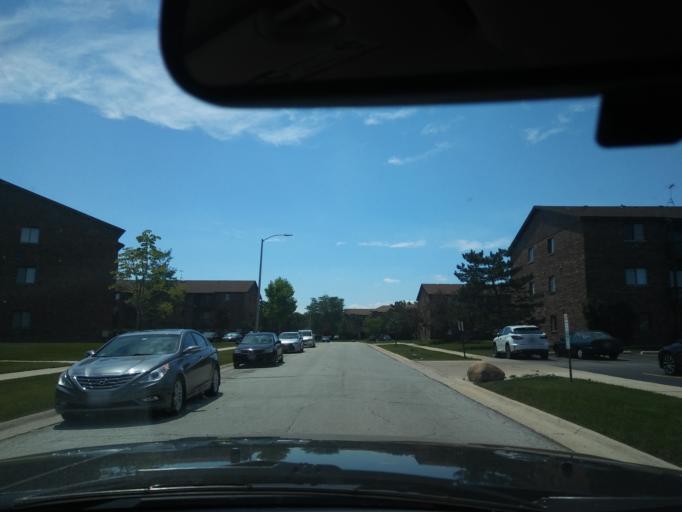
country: US
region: Illinois
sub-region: Cook County
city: Oak Forest
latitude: 41.6059
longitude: -87.7604
